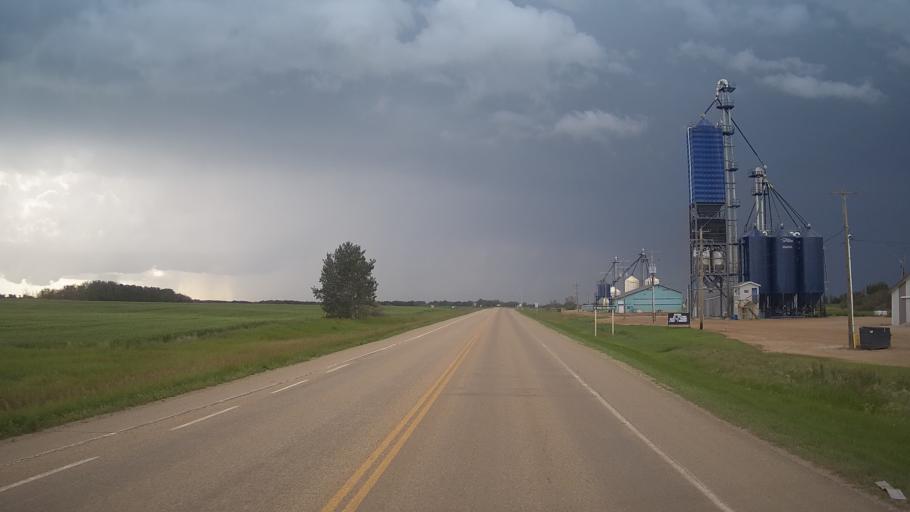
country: CA
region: Alberta
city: Tofield
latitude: 53.2882
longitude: -112.4344
